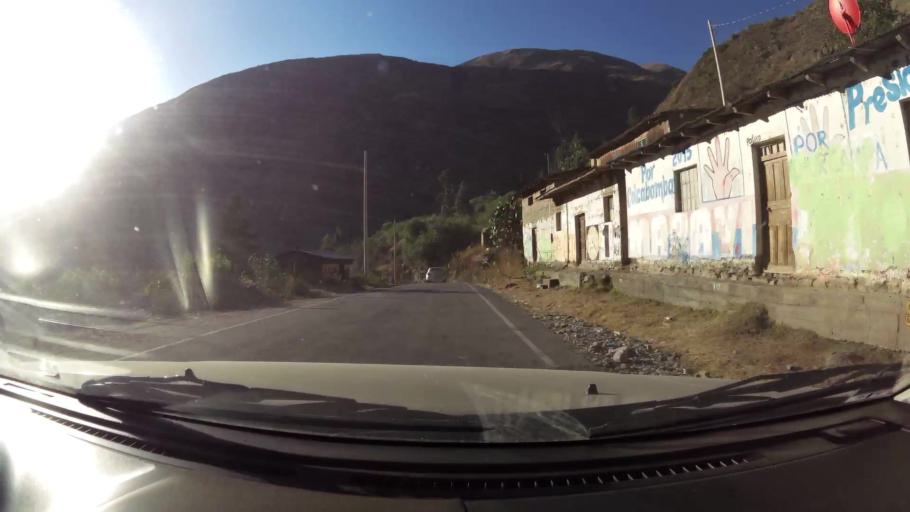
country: PE
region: Huancavelica
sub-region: Provincia de Tayacaja
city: Colcabamba
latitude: -12.5237
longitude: -74.6908
